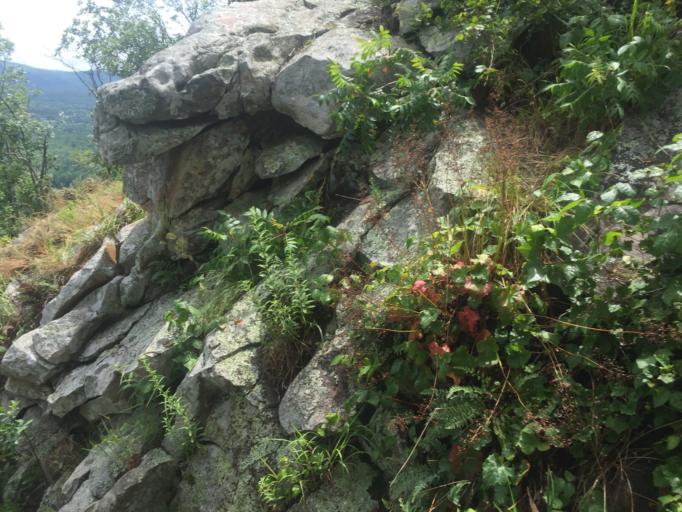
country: US
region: Arkansas
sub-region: Pulaski County
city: Maumelle
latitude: 34.8412
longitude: -92.4850
